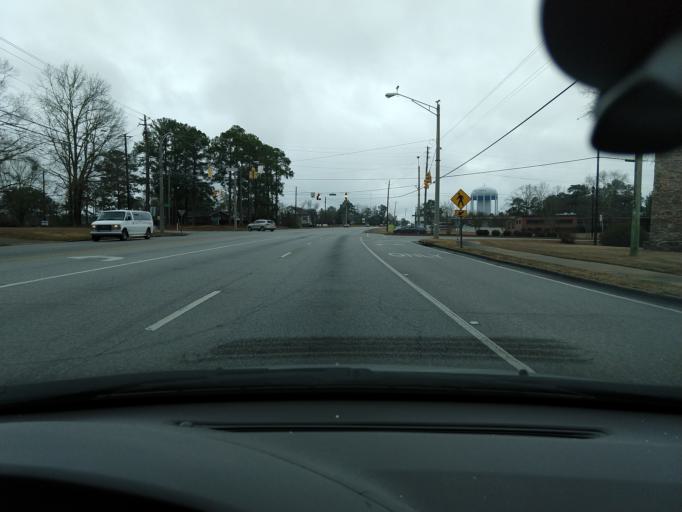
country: US
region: Alabama
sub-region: Houston County
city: Dothan
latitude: 31.2400
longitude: -85.4350
